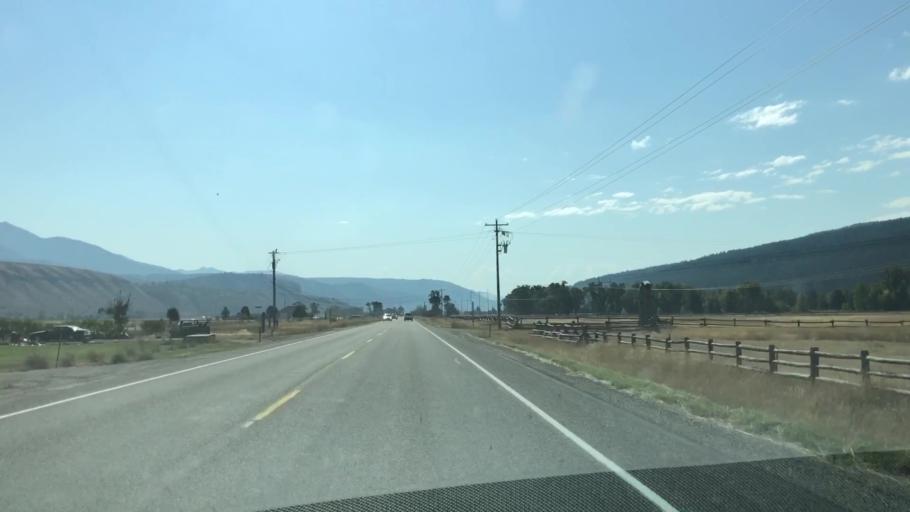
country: US
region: Idaho
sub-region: Teton County
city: Victor
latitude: 43.3971
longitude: -111.2810
